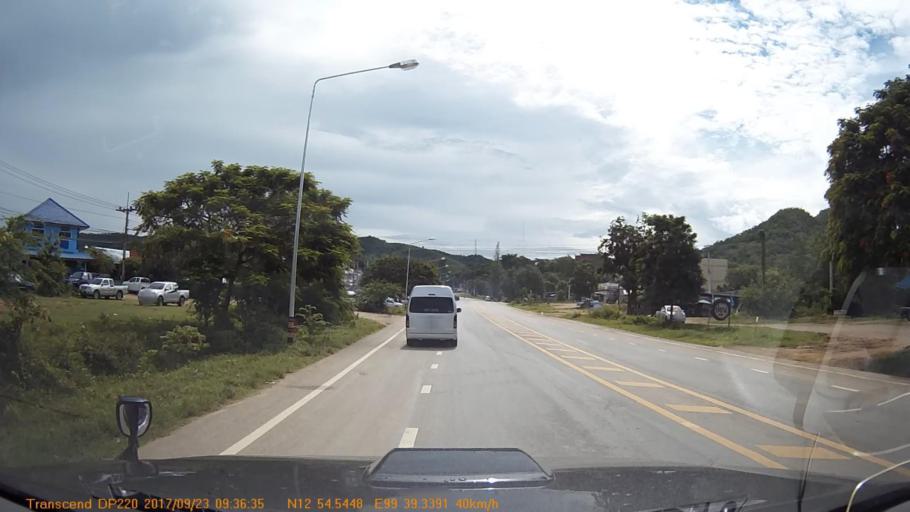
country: TH
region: Phetchaburi
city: Kaeng Krachan
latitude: 12.9090
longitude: 99.6554
